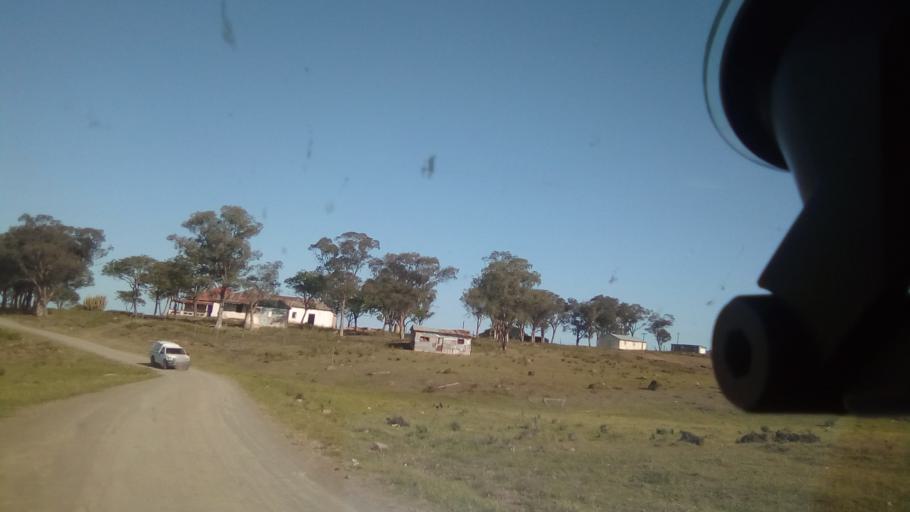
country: ZA
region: Eastern Cape
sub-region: Buffalo City Metropolitan Municipality
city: Bhisho
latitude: -32.8138
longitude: 27.3600
